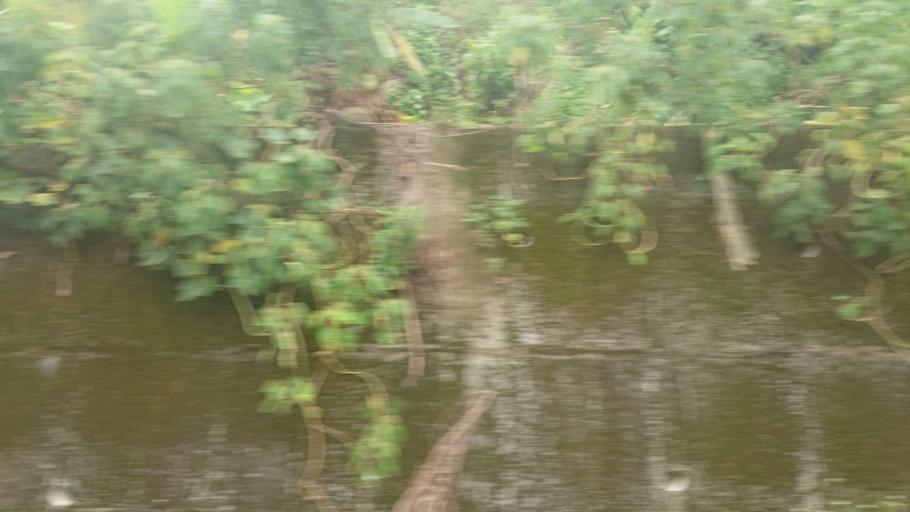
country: TW
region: Taiwan
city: Lugu
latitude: 23.8177
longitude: 120.8496
